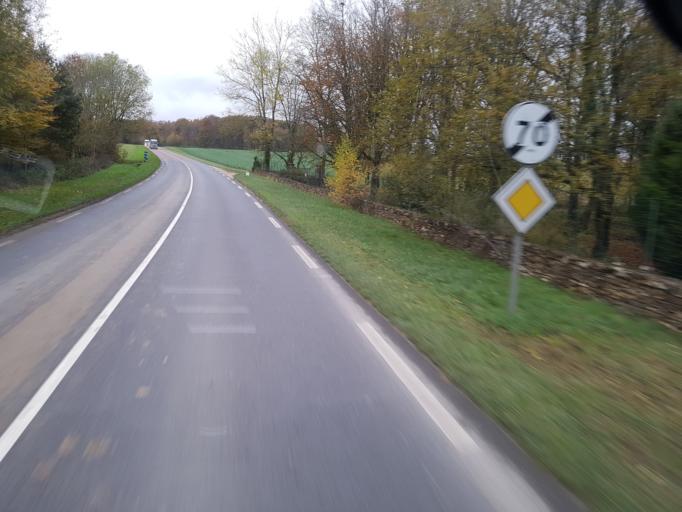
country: FR
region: Champagne-Ardenne
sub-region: Departement de la Marne
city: Esternay
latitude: 48.7915
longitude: 3.6348
